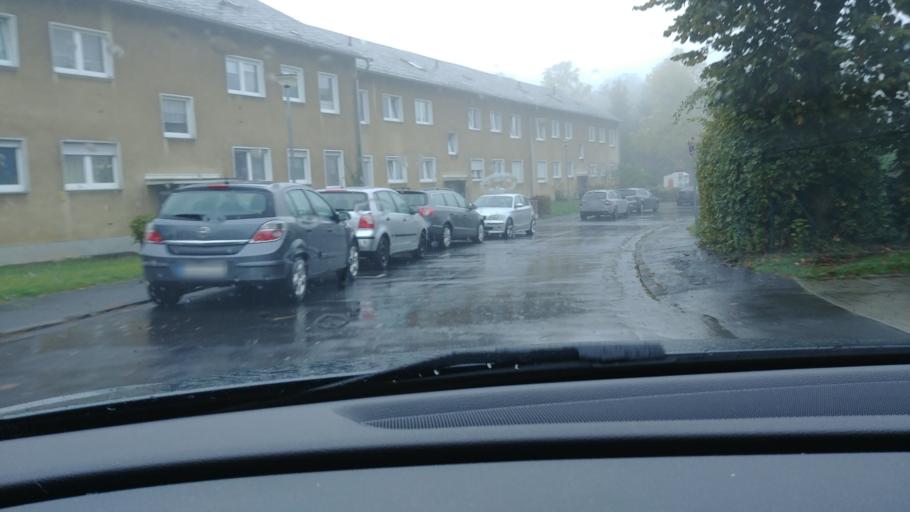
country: DE
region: Rheinland-Pfalz
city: Dohr
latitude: 50.1356
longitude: 7.1330
